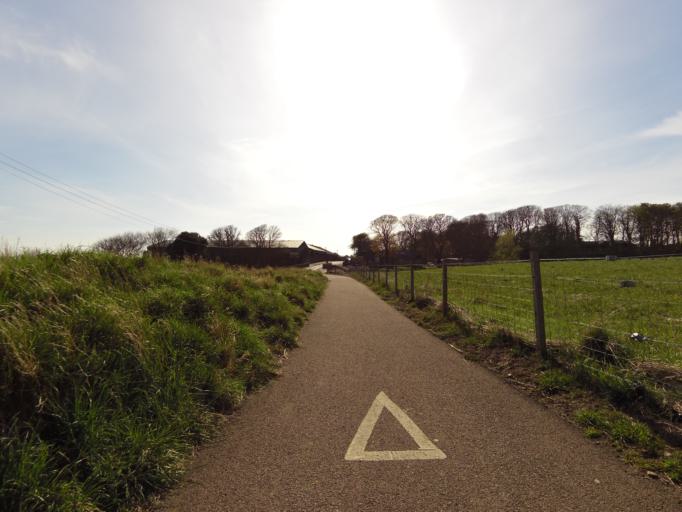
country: GB
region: Scotland
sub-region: Angus
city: Carnoustie
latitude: 56.5084
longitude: -2.6826
